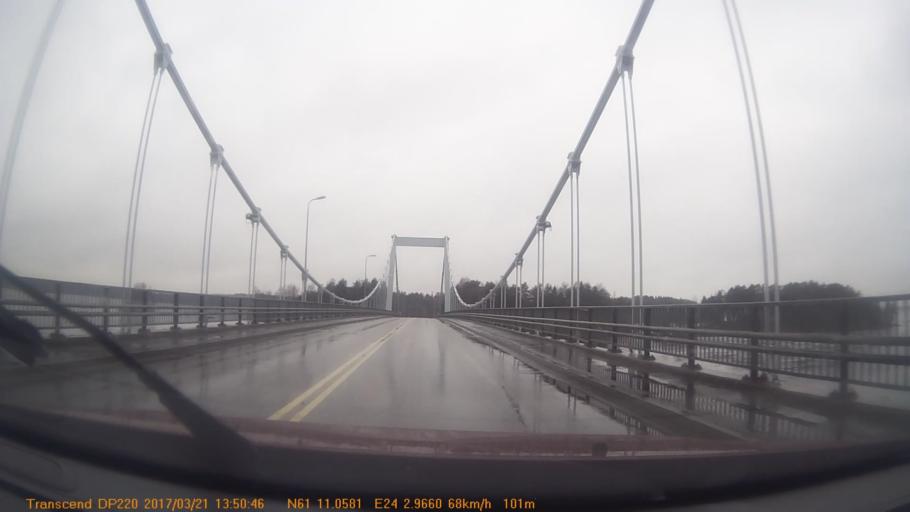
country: FI
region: Pirkanmaa
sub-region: Etelae-Pirkanmaa
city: Valkeakoski
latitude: 61.1844
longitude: 24.0498
